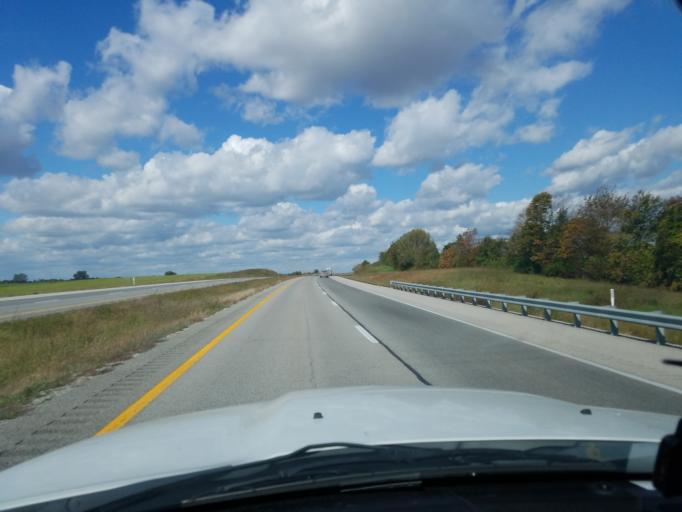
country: US
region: Kentucky
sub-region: Daviess County
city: Masonville
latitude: 37.6722
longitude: -87.0257
